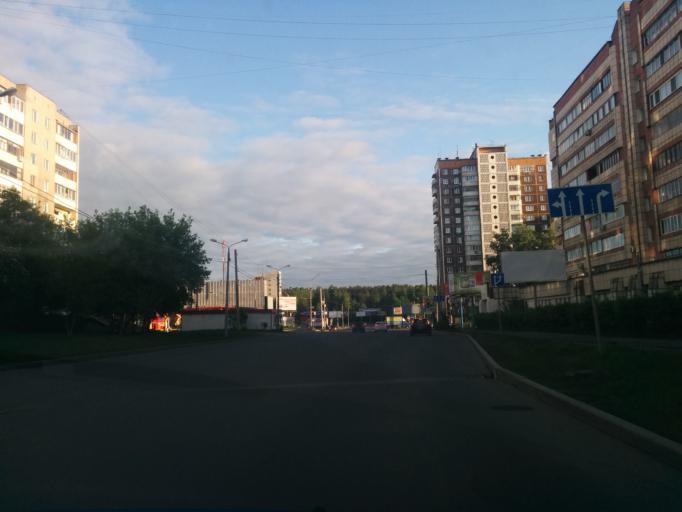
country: RU
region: Perm
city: Kondratovo
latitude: 57.9991
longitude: 56.1674
